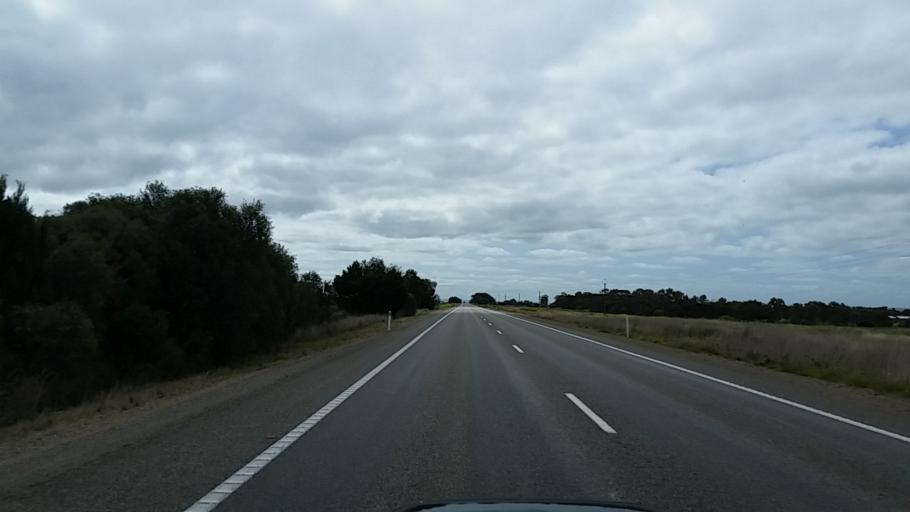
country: AU
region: South Australia
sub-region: Port Pirie City and Dists
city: Crystal Brook
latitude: -33.6426
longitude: 138.2273
